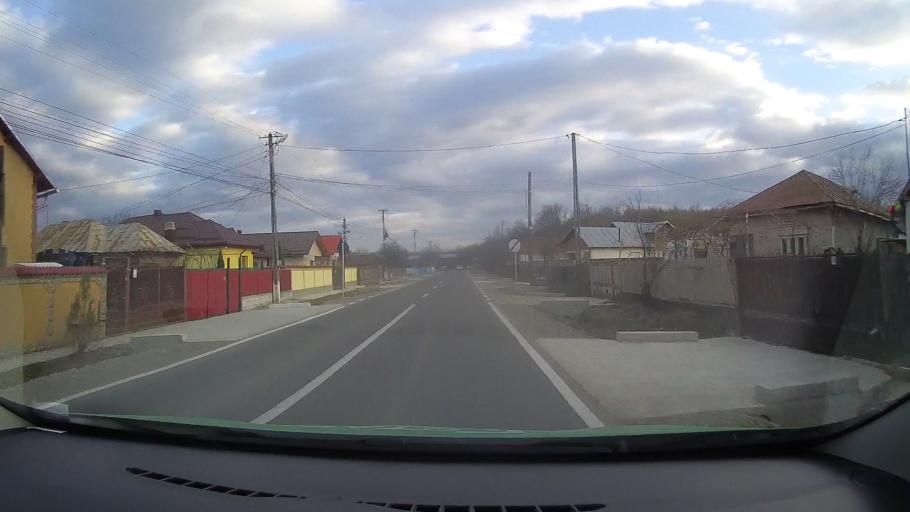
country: RO
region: Dambovita
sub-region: Comuna I. L. Caragiale
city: Mija
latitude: 44.9189
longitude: 25.6886
